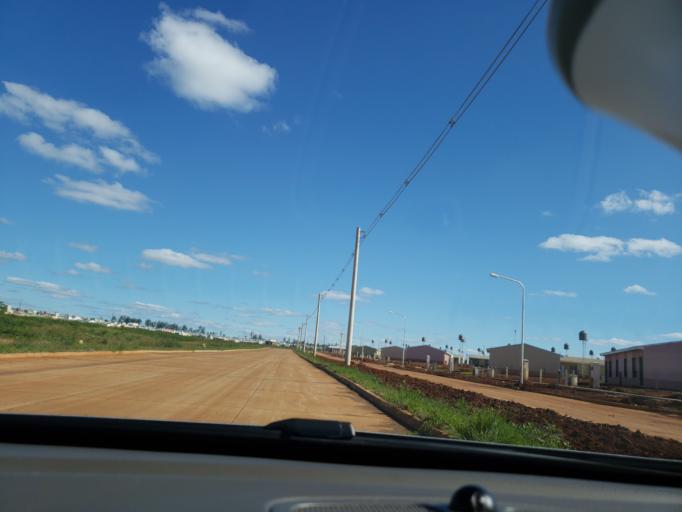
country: AR
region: Misiones
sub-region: Departamento de Capital
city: Posadas
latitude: -27.4006
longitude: -55.9891
